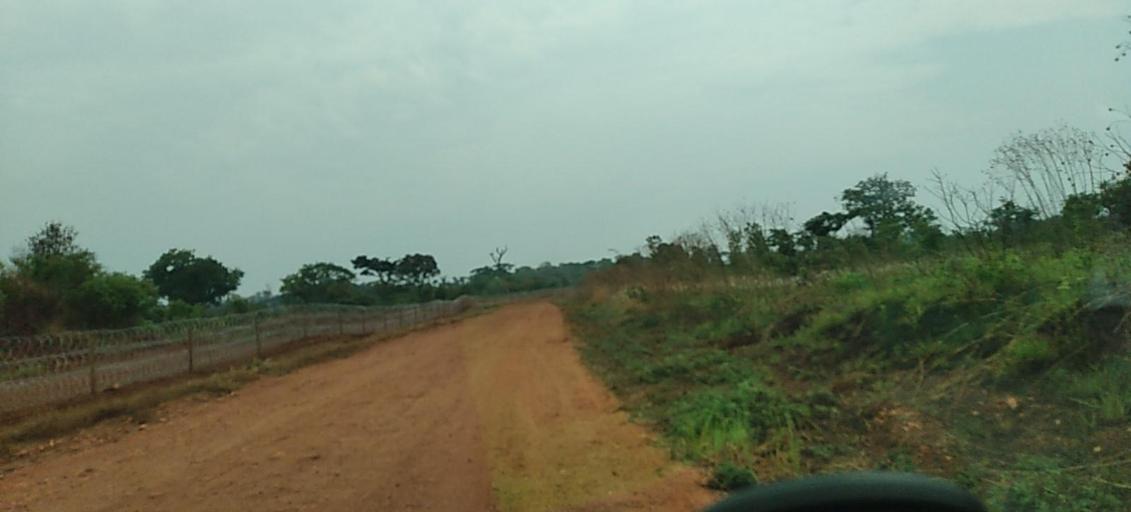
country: ZM
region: North-Western
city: Kansanshi
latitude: -12.1022
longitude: 26.4908
